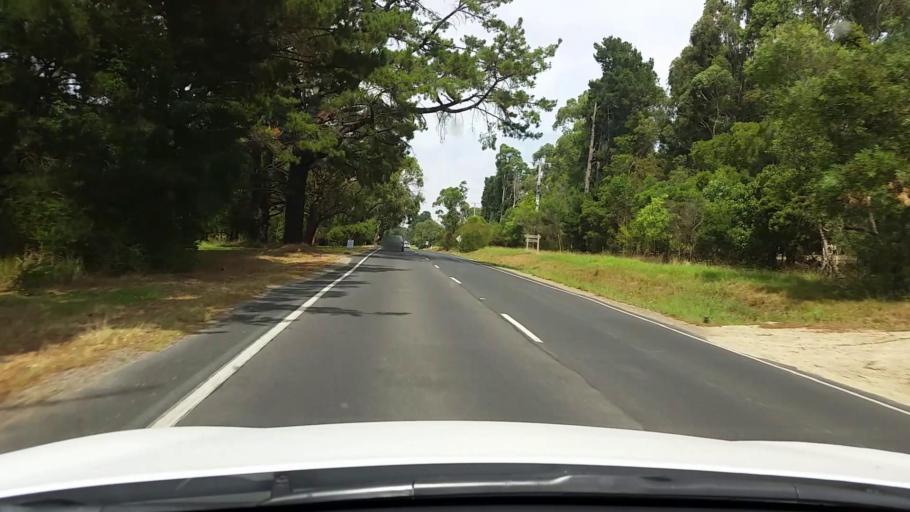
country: AU
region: Victoria
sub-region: Mornington Peninsula
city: Balnarring
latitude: -38.3672
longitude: 145.1364
